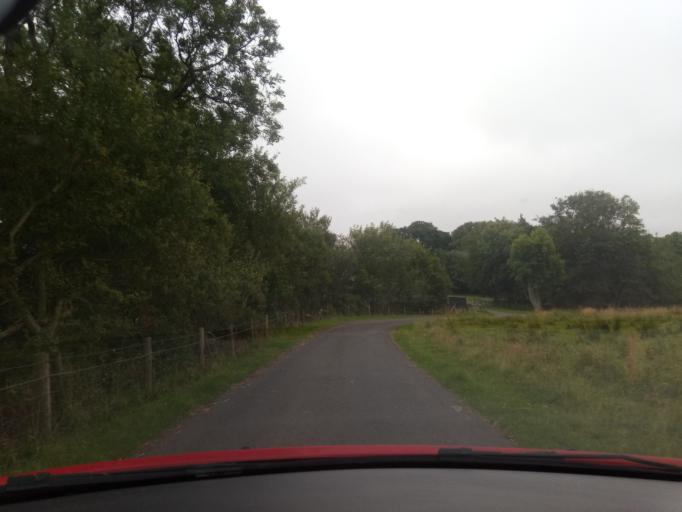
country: GB
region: England
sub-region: Northumberland
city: Otterburn
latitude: 55.2789
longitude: -2.0950
